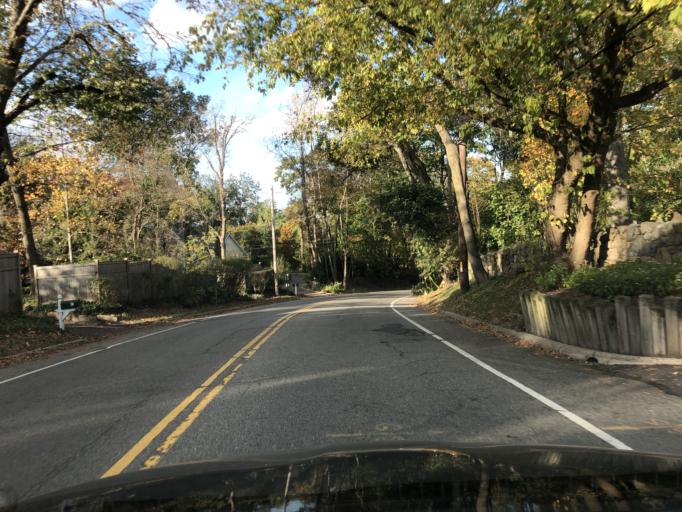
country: US
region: New York
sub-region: Nassau County
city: Roslyn Harbor
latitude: 40.8201
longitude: -73.6438
